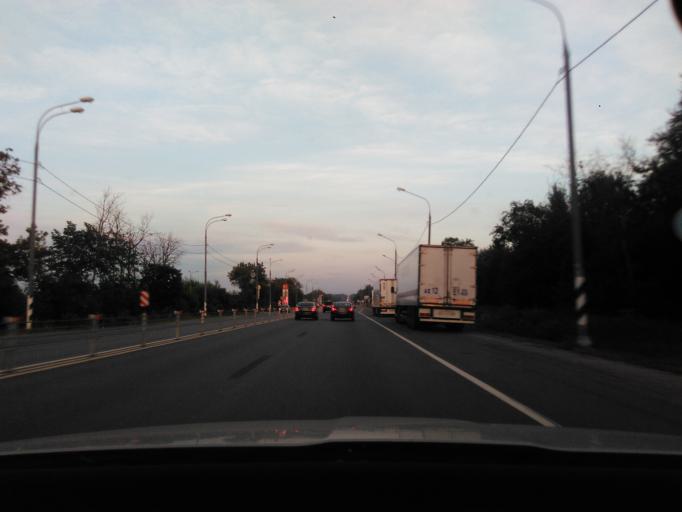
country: RU
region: Moskovskaya
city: Klin
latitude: 56.3099
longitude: 36.7795
